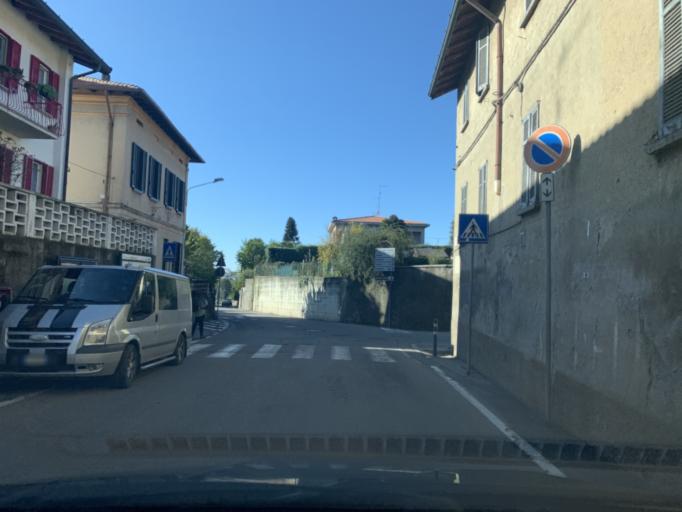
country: IT
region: Lombardy
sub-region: Provincia di Como
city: San Michele-San Giorgio
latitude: 45.6952
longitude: 9.0541
